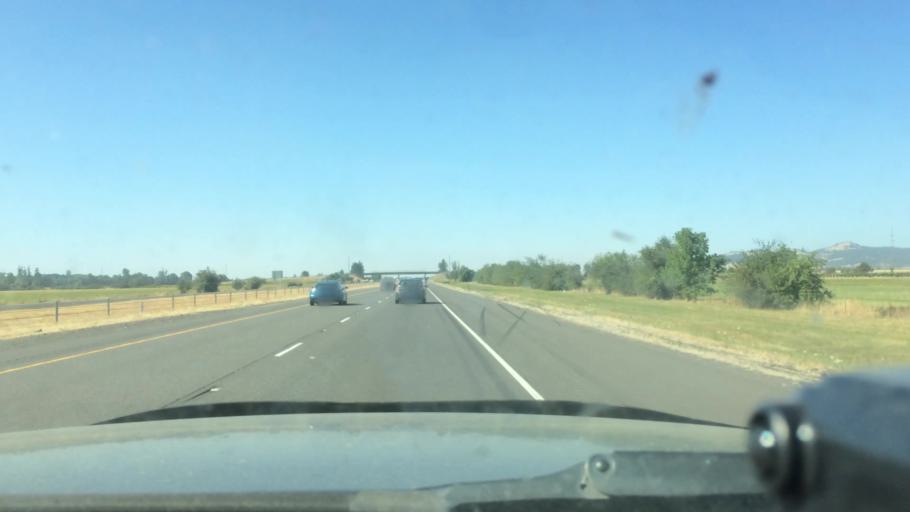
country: US
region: Oregon
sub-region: Lane County
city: Coburg
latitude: 44.2442
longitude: -123.0606
